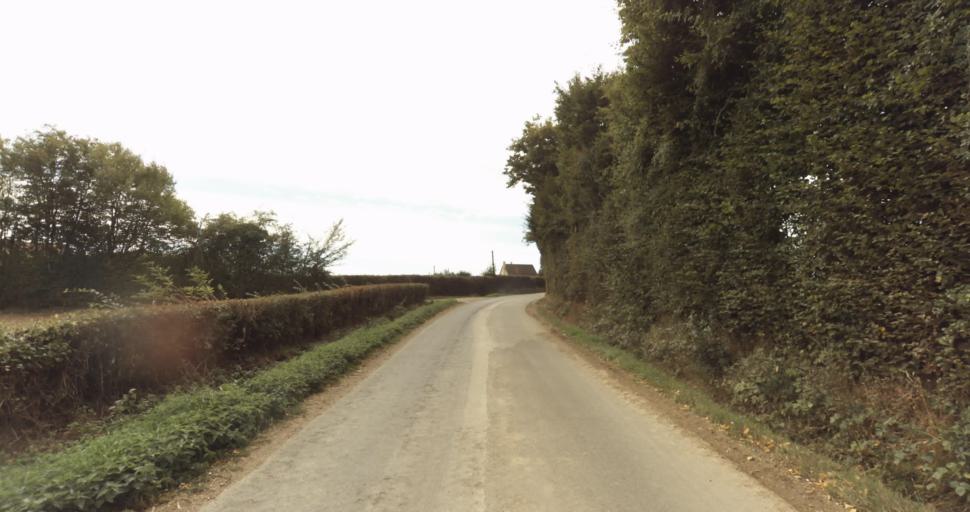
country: FR
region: Lower Normandy
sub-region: Departement du Calvados
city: La Vespiere
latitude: 48.9477
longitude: 0.3531
